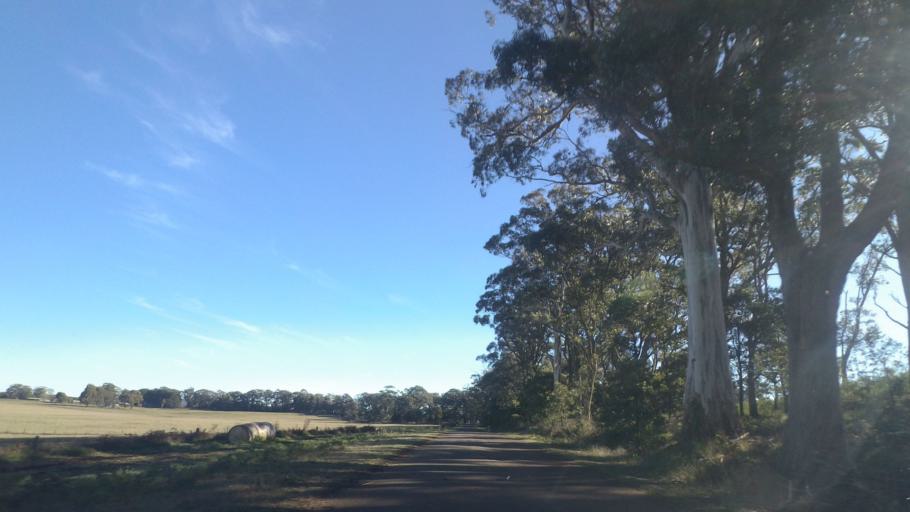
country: AU
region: Victoria
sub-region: Mount Alexander
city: Castlemaine
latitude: -37.3478
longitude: 144.2974
